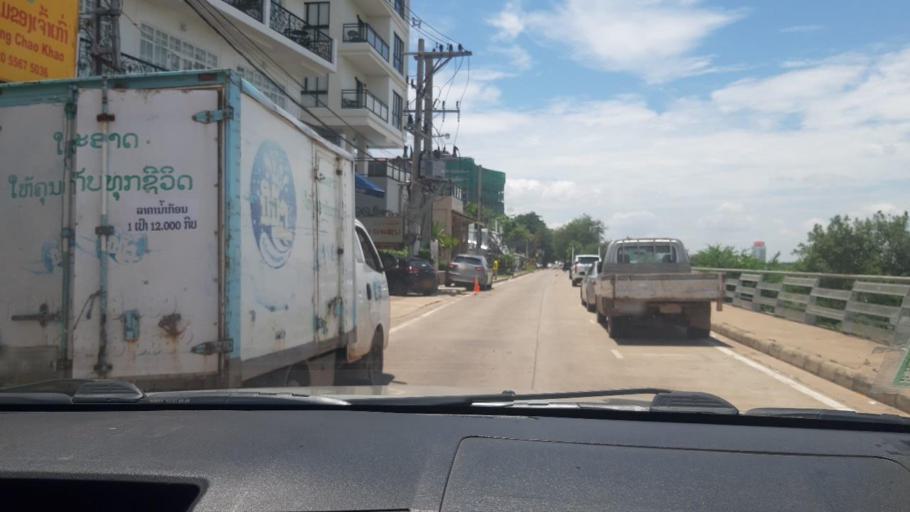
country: LA
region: Vientiane
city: Vientiane
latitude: 17.9658
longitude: 102.5965
